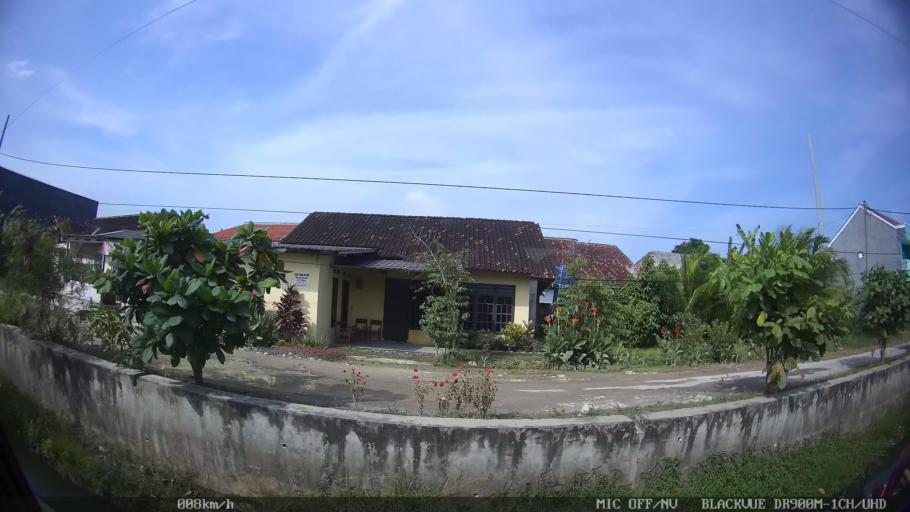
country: ID
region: Lampung
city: Kedaton
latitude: -5.3787
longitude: 105.2998
